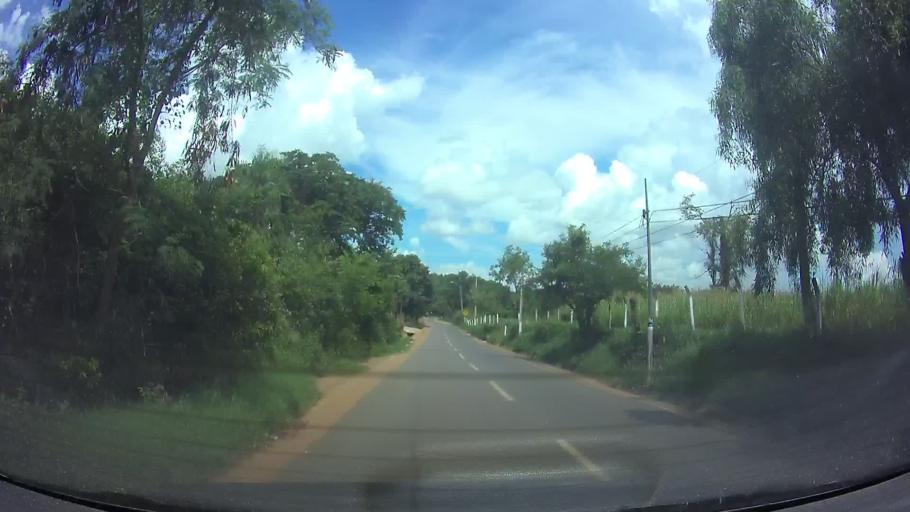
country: PY
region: Central
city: San Lorenzo
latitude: -25.3047
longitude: -57.4930
